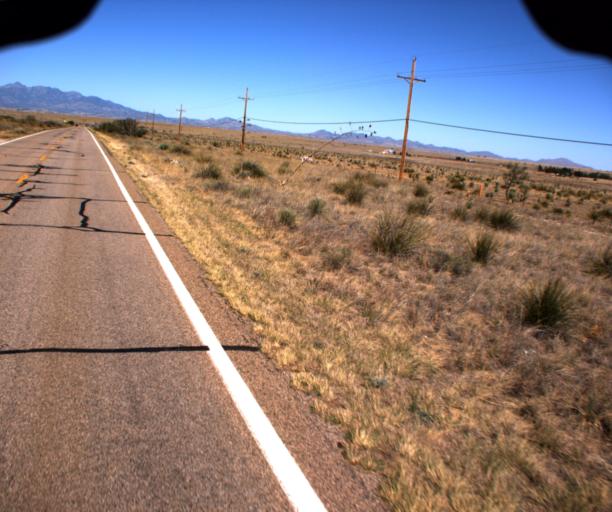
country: US
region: Arizona
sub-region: Cochise County
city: Huachuca City
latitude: 31.7240
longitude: -110.5129
